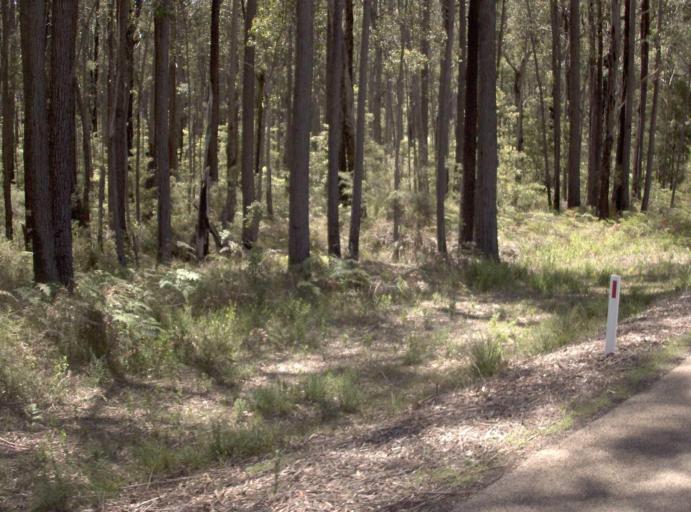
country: AU
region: Victoria
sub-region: East Gippsland
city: Lakes Entrance
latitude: -37.6694
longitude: 148.7984
